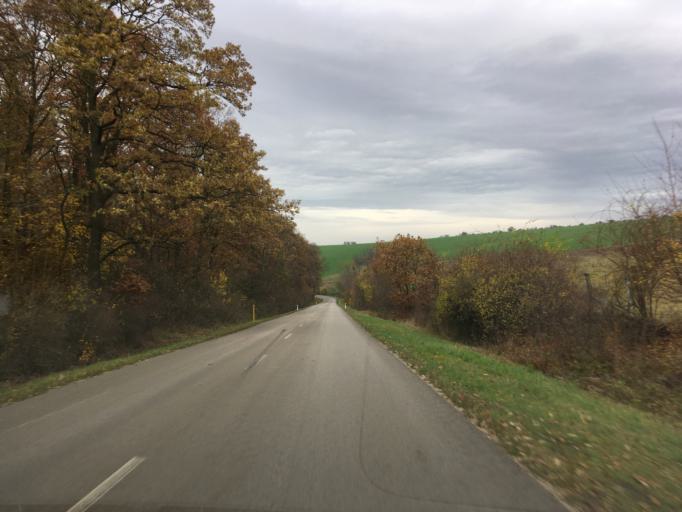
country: SK
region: Nitriansky
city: Svodin
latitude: 48.0324
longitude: 18.3893
